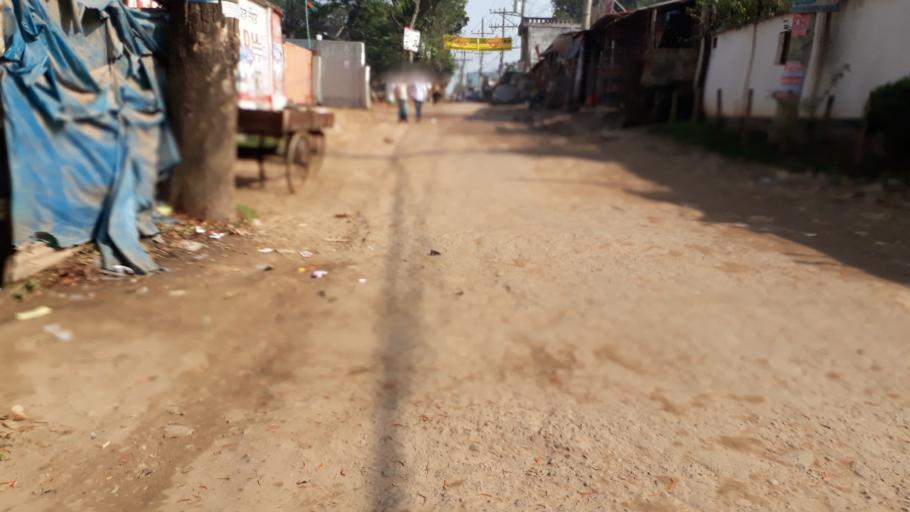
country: BD
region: Dhaka
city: Tungi
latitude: 23.8509
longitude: 90.2872
